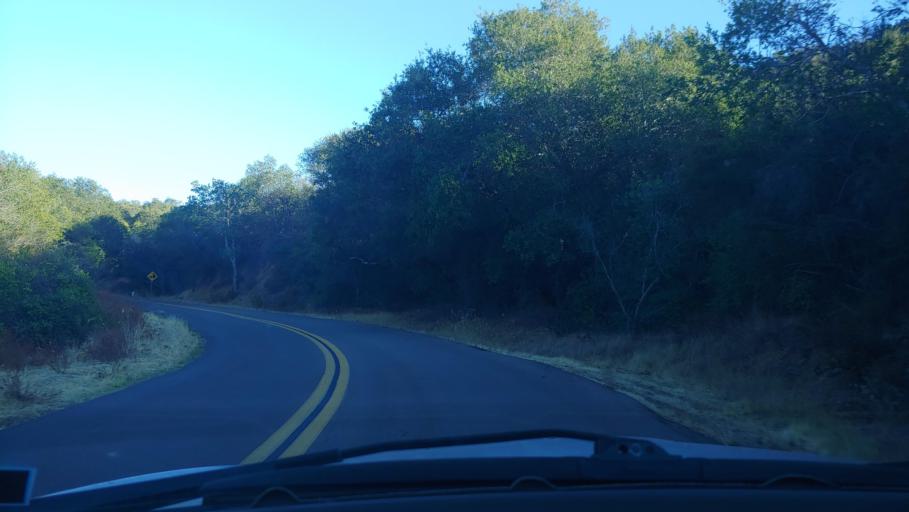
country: US
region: California
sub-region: Santa Barbara County
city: Goleta
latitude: 34.5356
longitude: -119.8481
